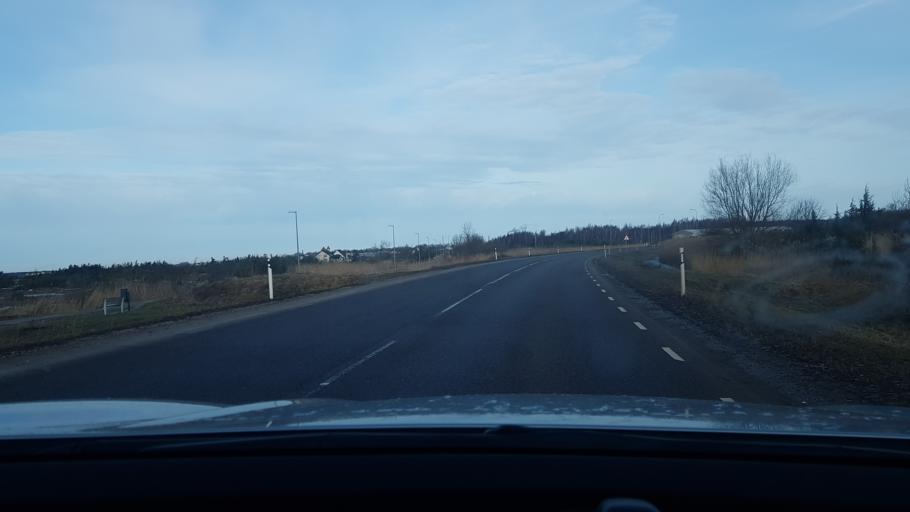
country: EE
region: Saare
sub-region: Kuressaare linn
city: Kuressaare
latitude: 58.2344
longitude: 22.5012
